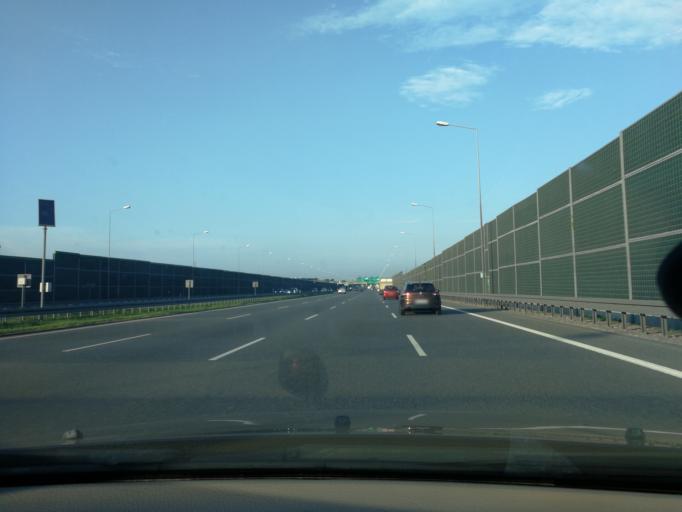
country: PL
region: Masovian Voivodeship
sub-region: Powiat pruszkowski
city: Piastow
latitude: 52.1941
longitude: 20.8213
